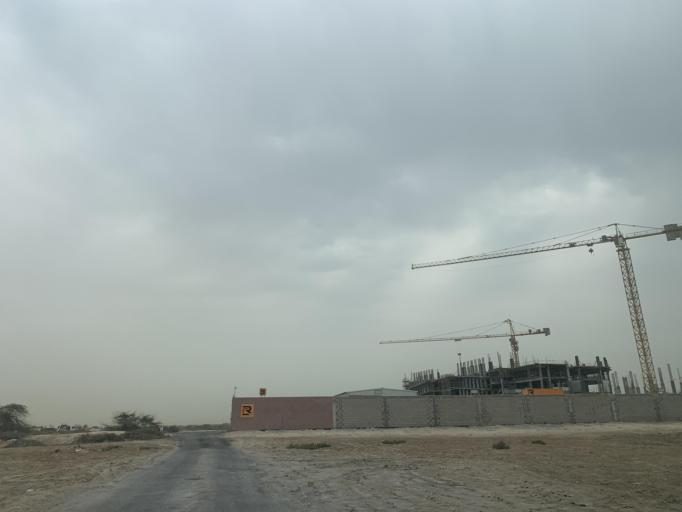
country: BH
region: Northern
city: Madinat `Isa
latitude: 26.1781
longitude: 50.5045
